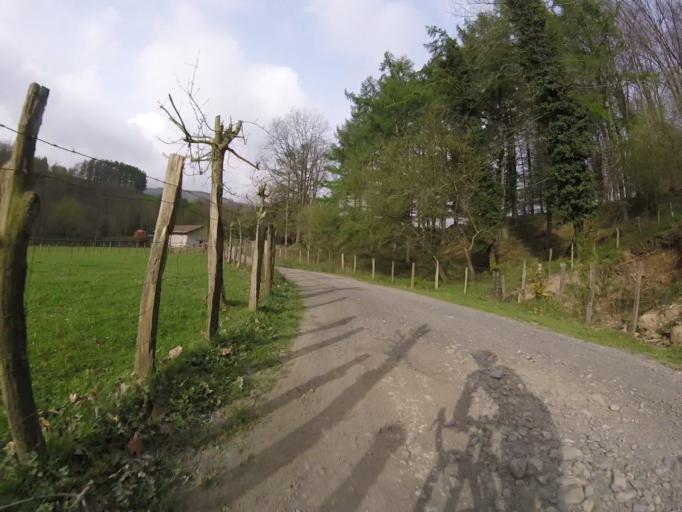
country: ES
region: Navarre
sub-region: Provincia de Navarra
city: Areso
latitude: 43.1074
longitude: -1.9539
